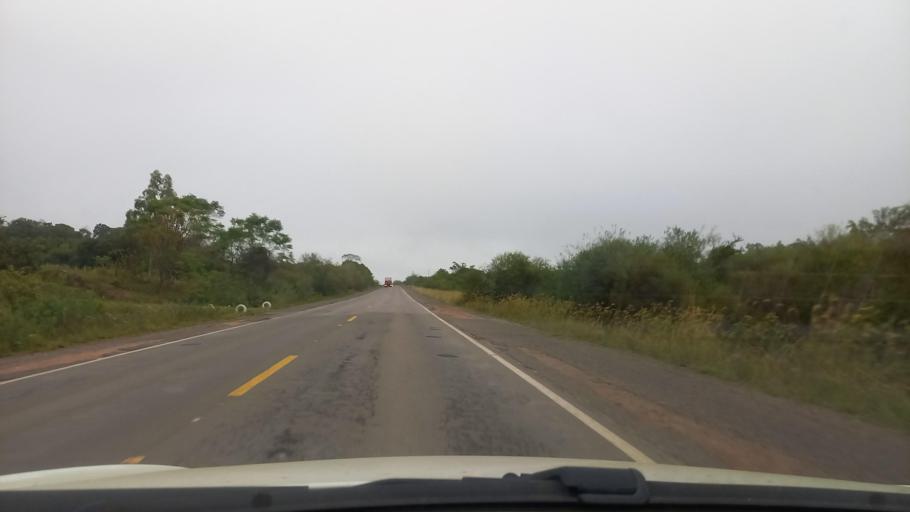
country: BR
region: Rio Grande do Sul
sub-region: Cacequi
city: Cacequi
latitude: -30.1232
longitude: -54.6459
